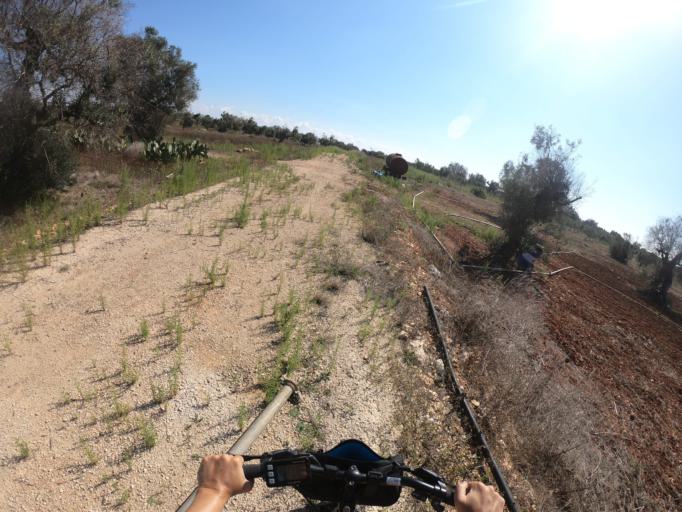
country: IT
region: Apulia
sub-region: Provincia di Lecce
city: Galatone
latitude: 40.1322
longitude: 18.0735
